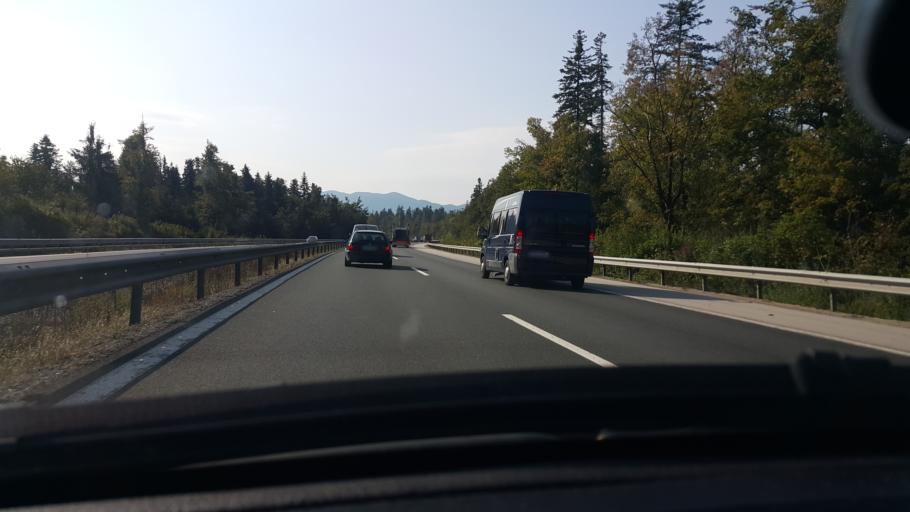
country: SI
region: Logatec
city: Logatec
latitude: 45.8819
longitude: 14.2627
